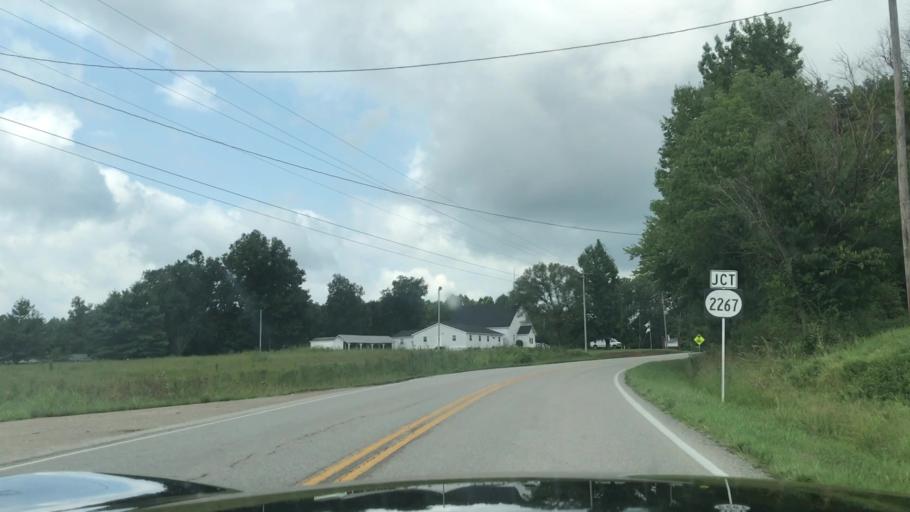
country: US
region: Kentucky
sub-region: Butler County
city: Morgantown
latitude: 37.1887
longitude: -86.7552
